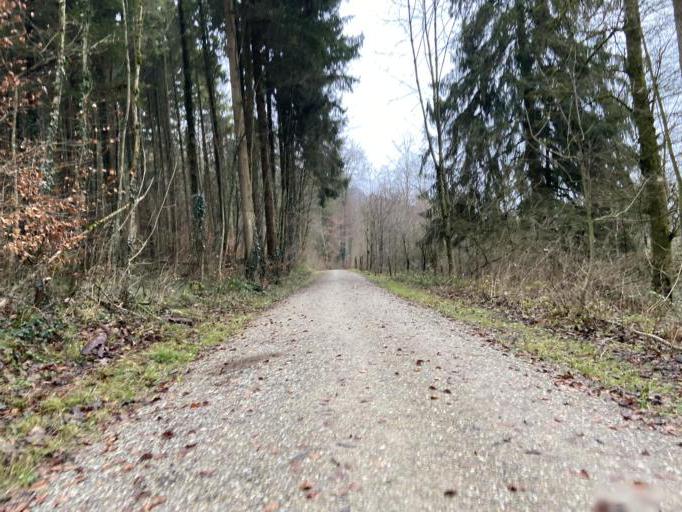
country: CH
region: Zurich
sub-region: Bezirk Winterthur
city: Toess (Kreis 4) / Vorder-Daettnau
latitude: 47.4849
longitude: 8.6872
